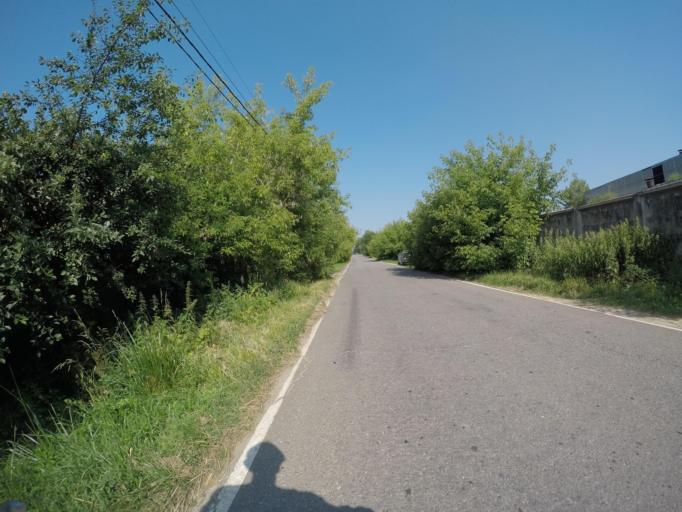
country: RU
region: Moskovskaya
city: Rechitsy
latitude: 55.6166
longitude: 38.5325
